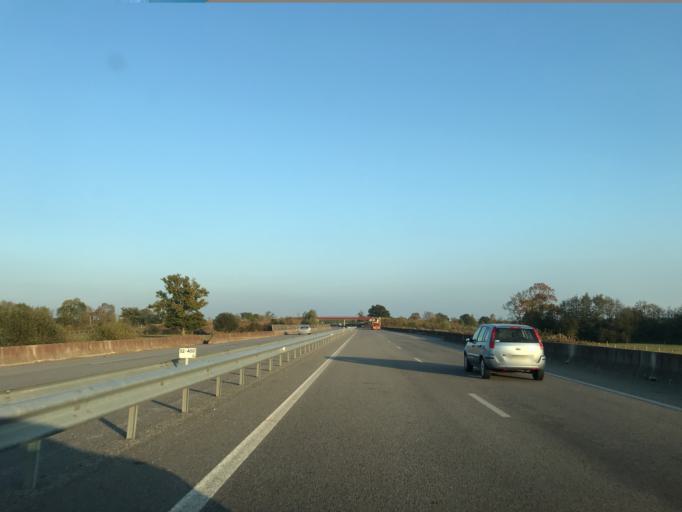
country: FR
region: Lower Normandy
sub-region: Departement de l'Orne
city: Valframbert
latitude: 48.4796
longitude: 0.2323
